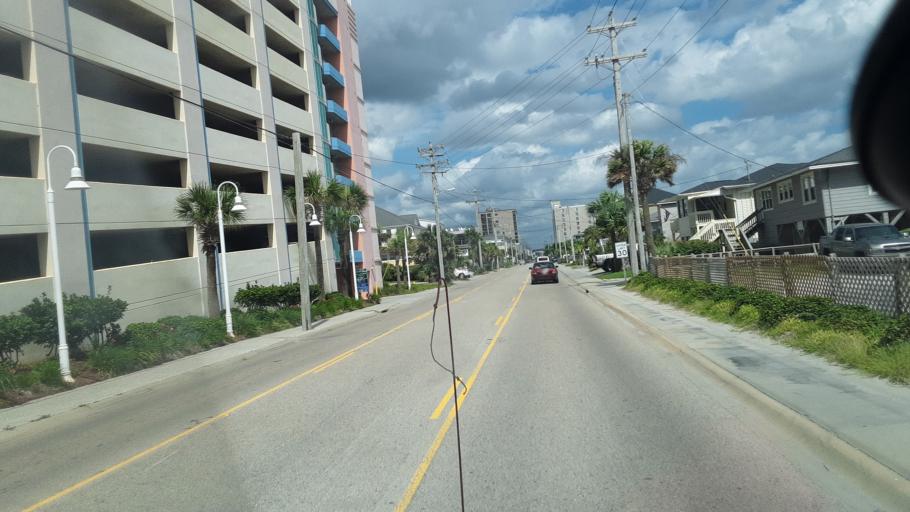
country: US
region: South Carolina
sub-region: Horry County
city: Little River
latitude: 33.8308
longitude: -78.6330
